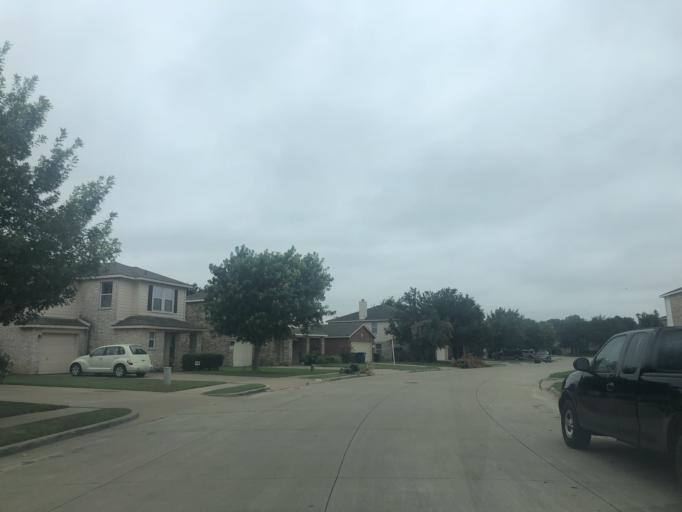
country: US
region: Texas
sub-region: Dallas County
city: Cockrell Hill
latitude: 32.7879
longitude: -96.8638
